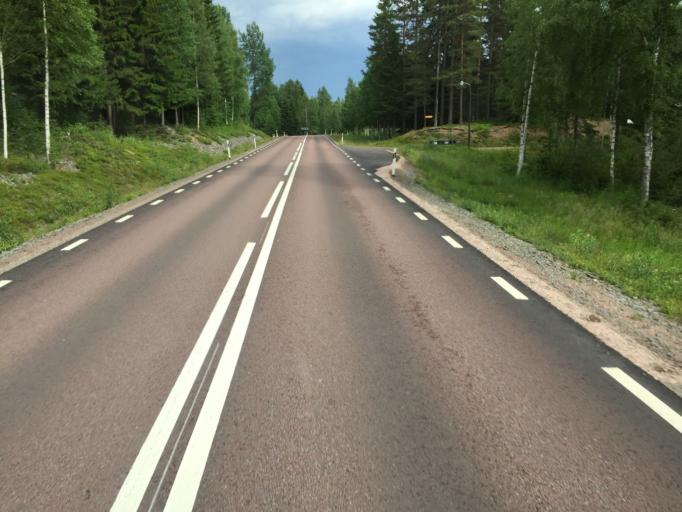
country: SE
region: Dalarna
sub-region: Vansbro Kommun
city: Vansbro
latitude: 60.8165
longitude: 14.1100
